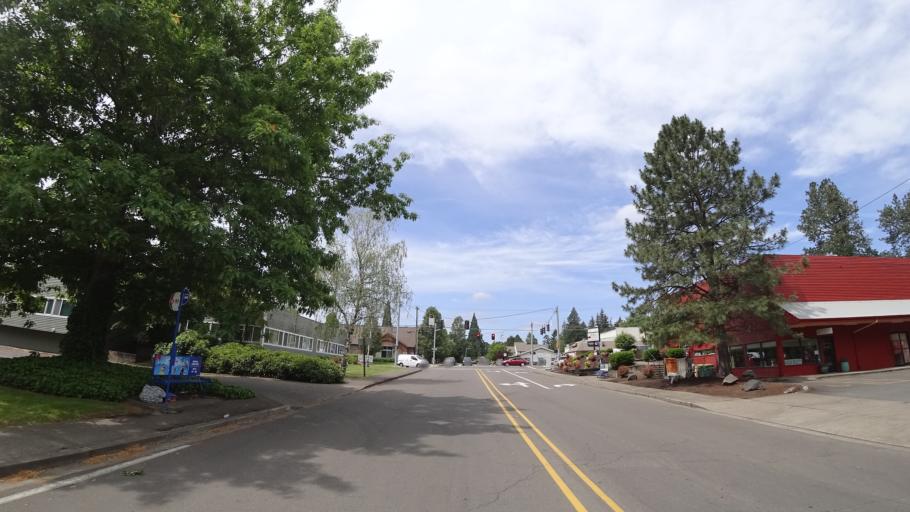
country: US
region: Oregon
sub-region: Washington County
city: Metzger
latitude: 45.4466
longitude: -122.7648
